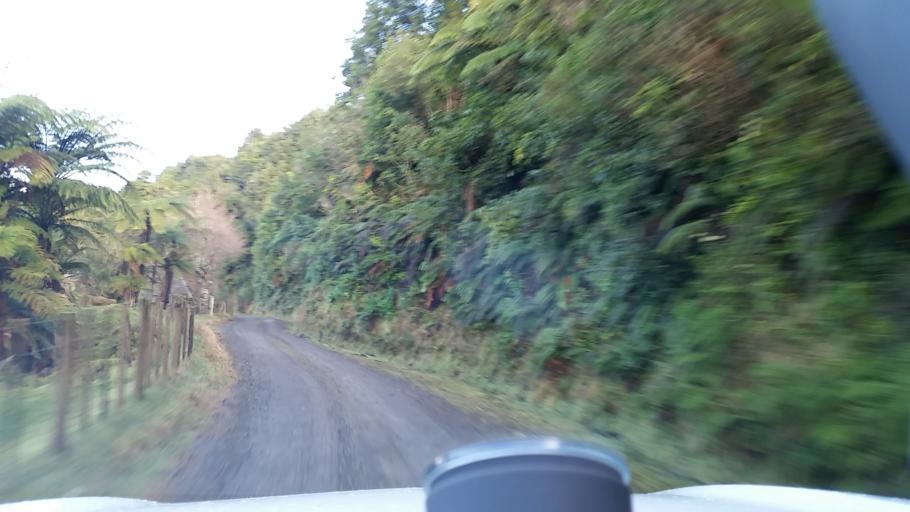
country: NZ
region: Taranaki
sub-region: South Taranaki District
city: Eltham
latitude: -39.4151
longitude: 174.5614
